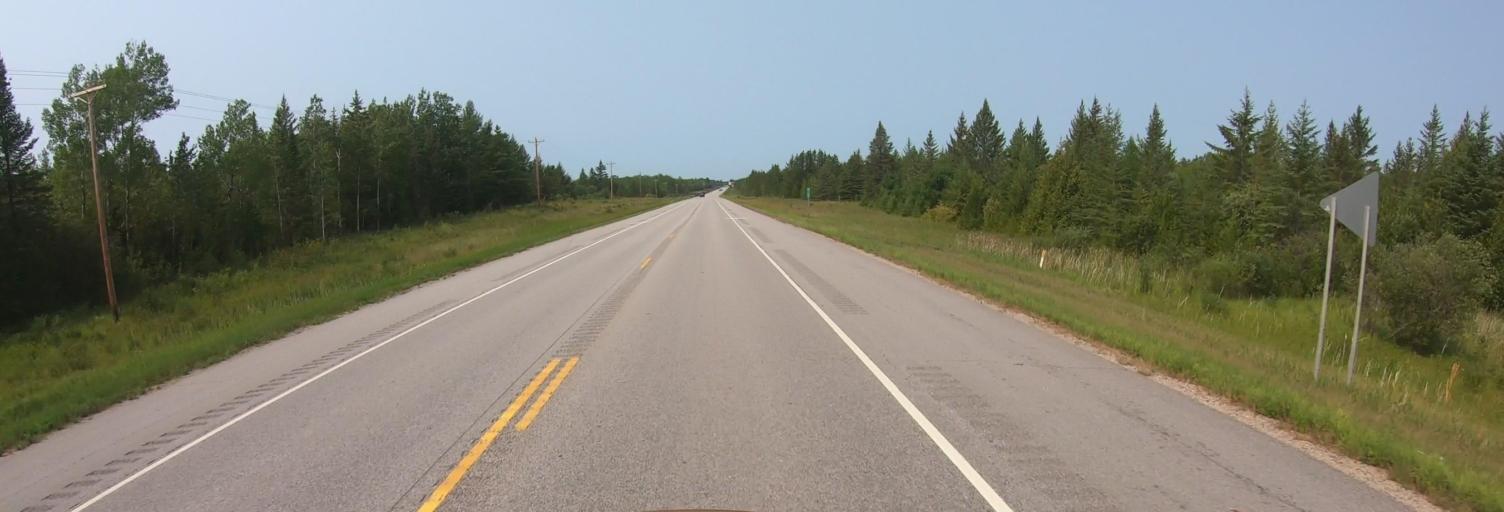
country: CA
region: Ontario
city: Fort Frances
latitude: 48.4101
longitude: -93.1742
